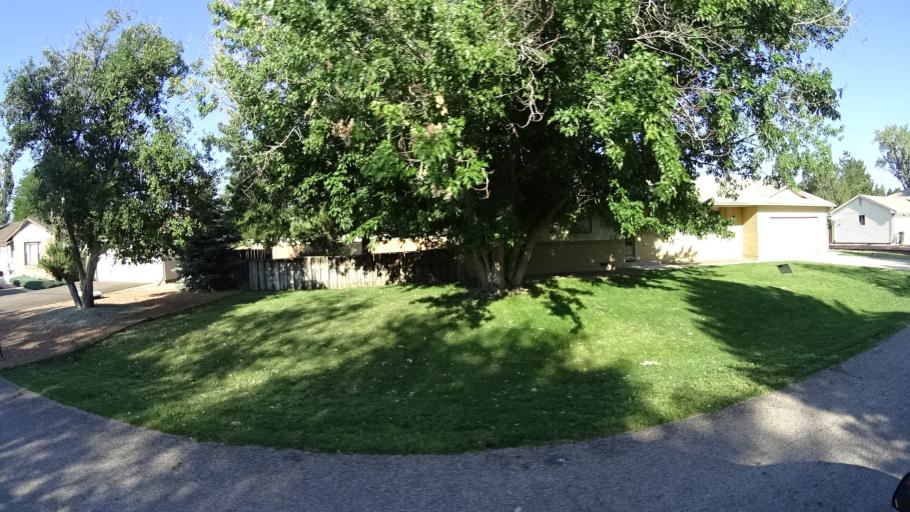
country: US
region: Colorado
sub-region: El Paso County
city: Air Force Academy
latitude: 38.9311
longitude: -104.8025
